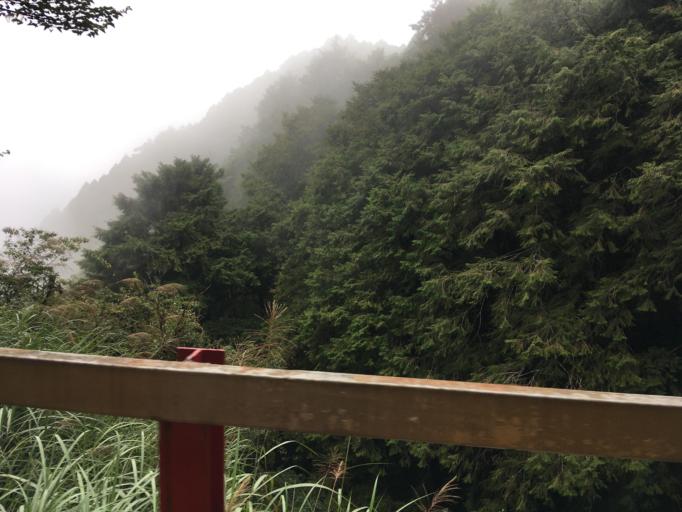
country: TW
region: Taiwan
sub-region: Yilan
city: Yilan
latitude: 24.4826
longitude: 121.5353
